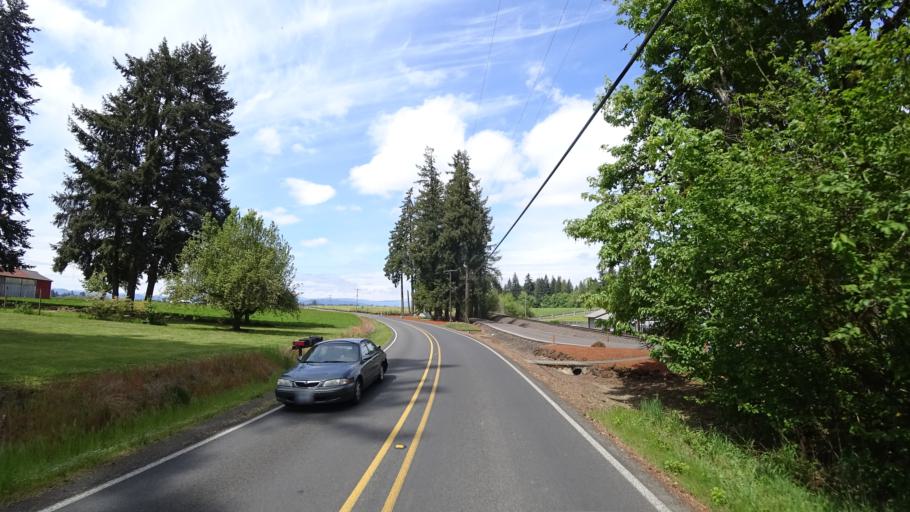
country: US
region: Oregon
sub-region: Washington County
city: Hillsboro
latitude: 45.5436
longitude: -123.0060
